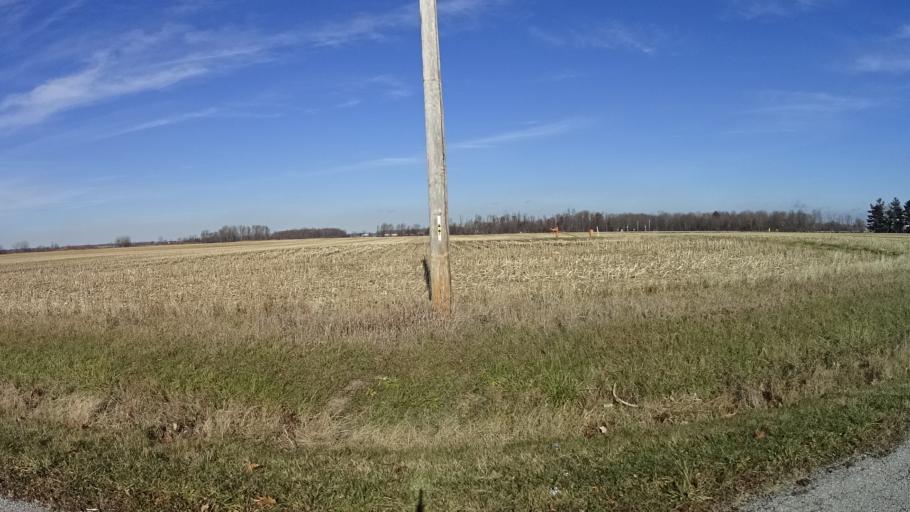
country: US
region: Ohio
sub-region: Lorain County
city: Wellington
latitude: 41.1306
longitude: -82.1825
